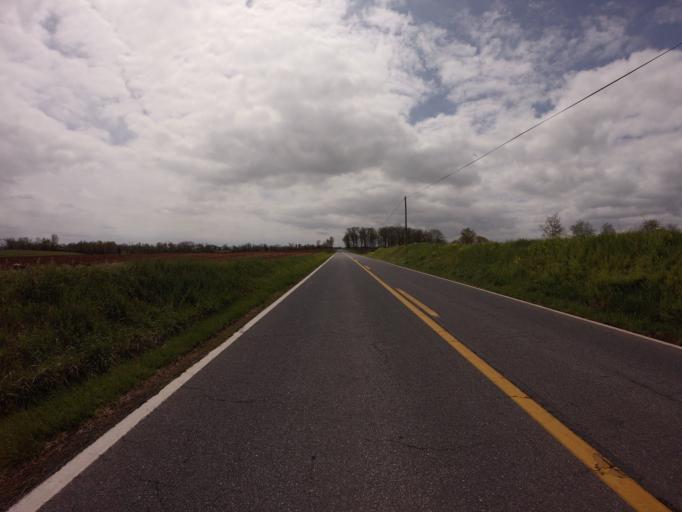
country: US
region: Maryland
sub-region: Frederick County
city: Thurmont
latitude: 39.5902
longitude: -77.3611
